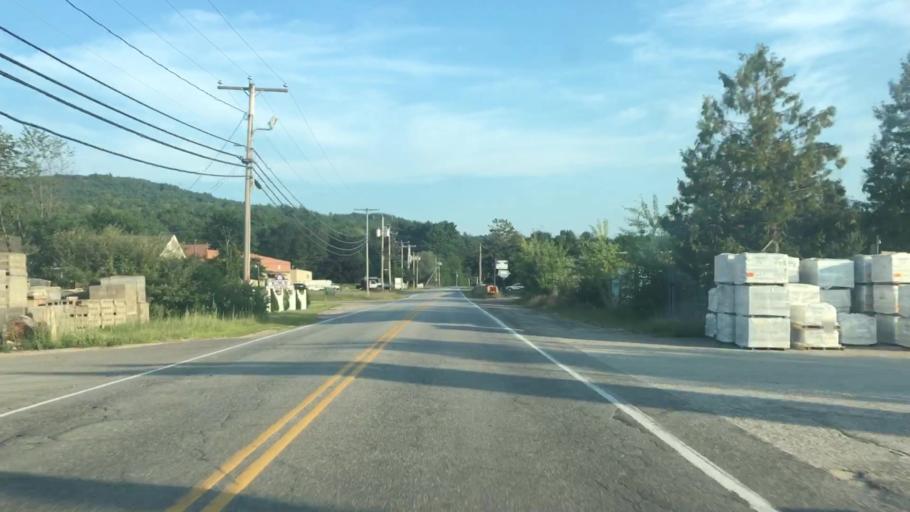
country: US
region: New Hampshire
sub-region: Belknap County
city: Laconia
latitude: 43.5109
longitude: -71.4522
